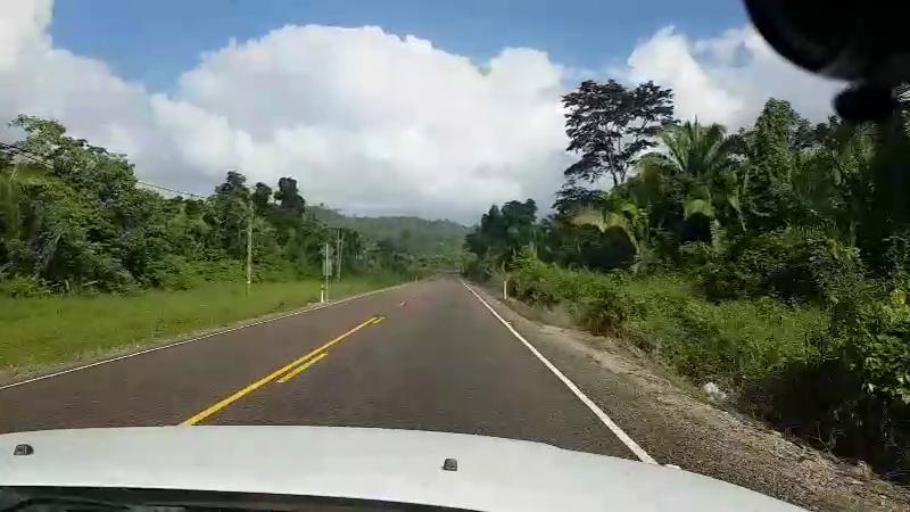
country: BZ
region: Cayo
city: Belmopan
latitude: 17.1463
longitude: -88.7281
